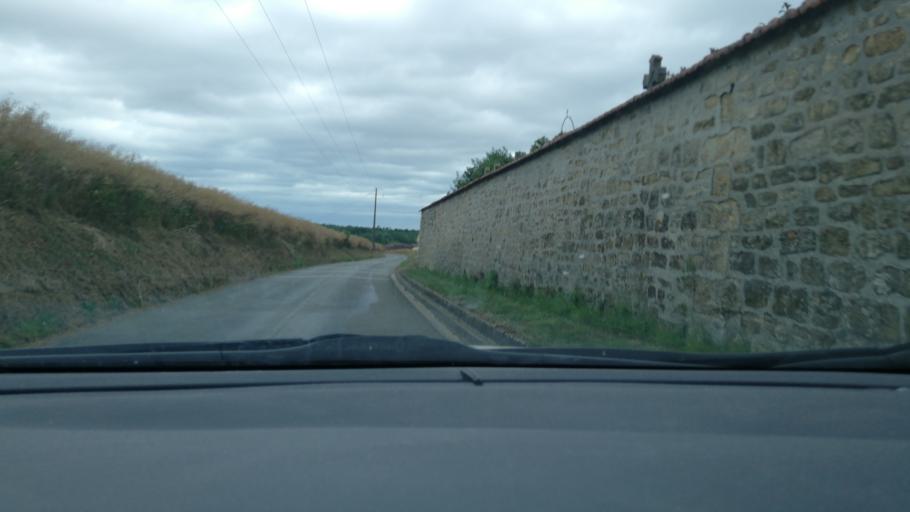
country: FR
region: Ile-de-France
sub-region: Departement du Val-d'Oise
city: Osny
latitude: 49.0913
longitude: 2.0728
